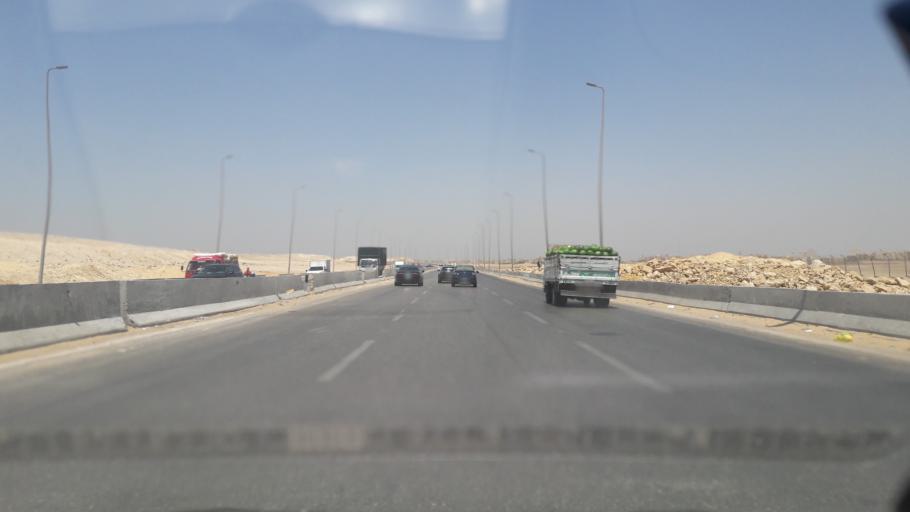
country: EG
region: Al Jizah
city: Al Jizah
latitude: 29.9691
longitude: 31.0704
